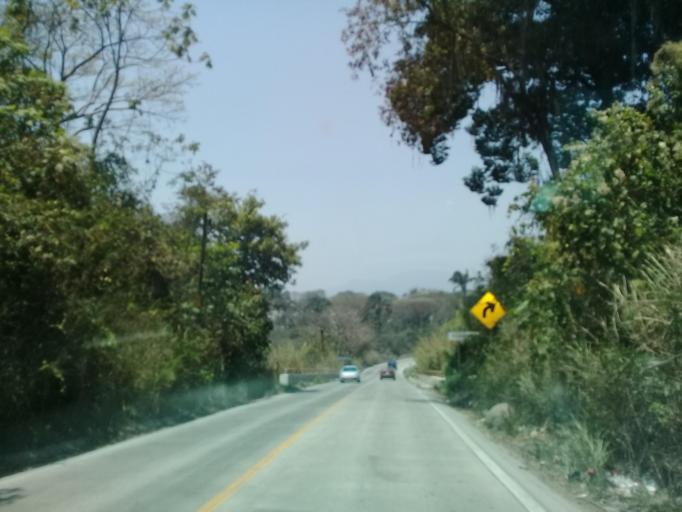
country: MX
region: Veracruz
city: Paraje Nuevo
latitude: 18.8690
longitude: -96.8762
